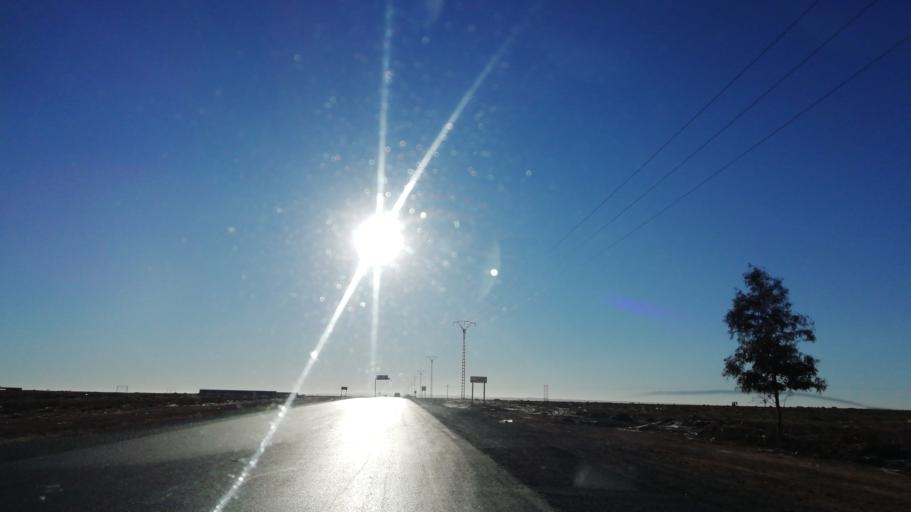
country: DZ
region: Saida
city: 'Ain el Hadjar
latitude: 34.0220
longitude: 0.1024
